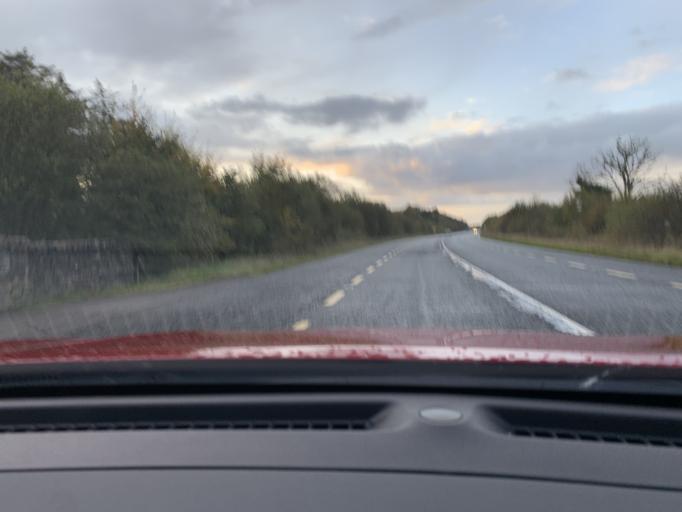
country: IE
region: Connaught
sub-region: County Leitrim
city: Carrick-on-Shannon
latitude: 53.9501
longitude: -8.1486
